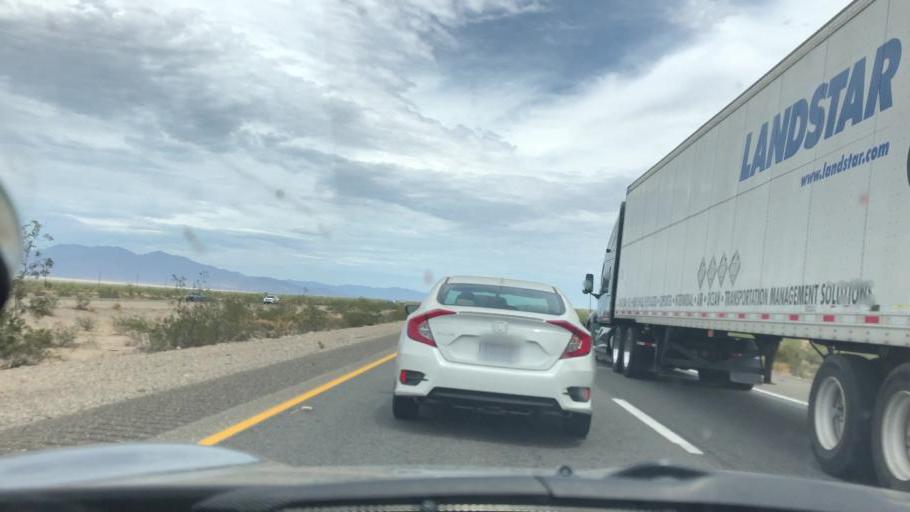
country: US
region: California
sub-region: Imperial County
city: Niland
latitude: 33.7095
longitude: -115.3717
